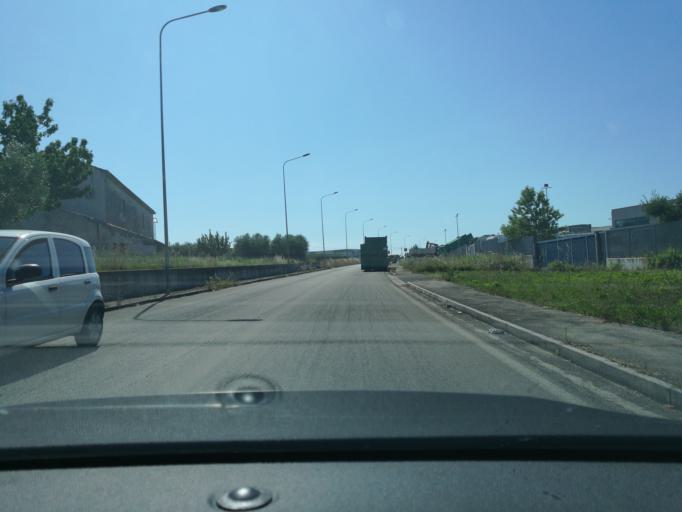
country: IT
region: Abruzzo
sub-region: Provincia di Chieti
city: Vasto
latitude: 42.1647
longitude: 14.6868
